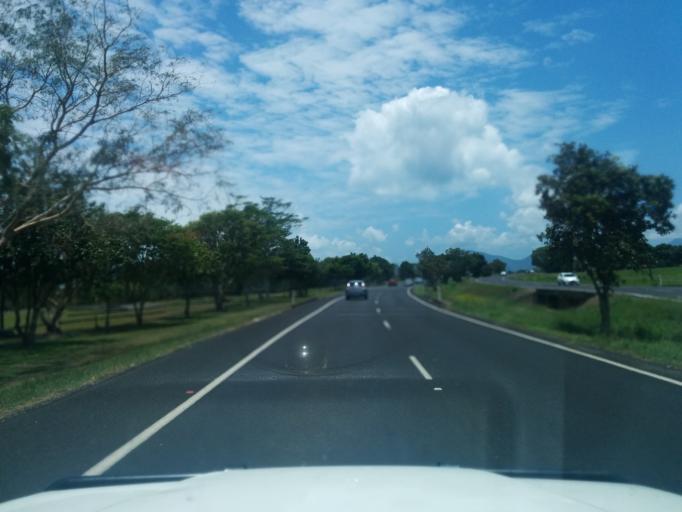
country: AU
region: Queensland
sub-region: Cairns
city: Redlynch
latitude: -16.8497
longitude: 145.7133
